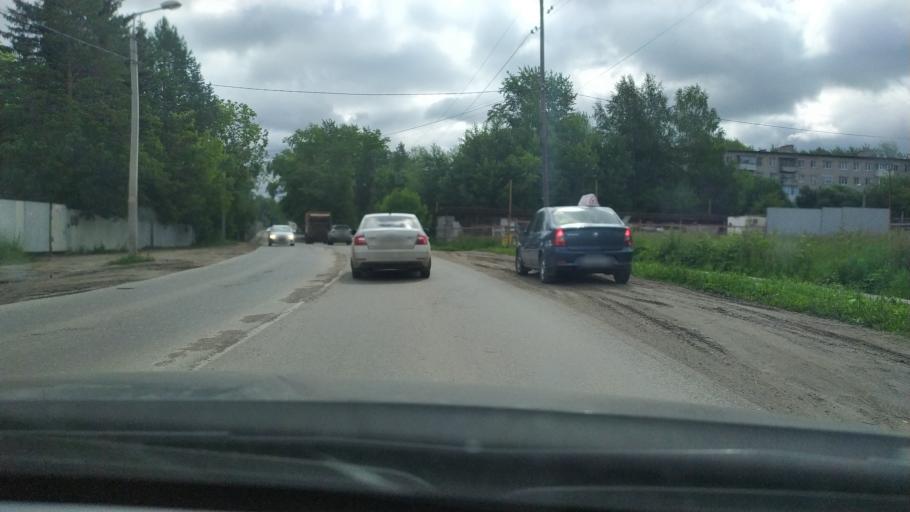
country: RU
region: Perm
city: Froly
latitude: 57.9762
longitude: 56.3162
